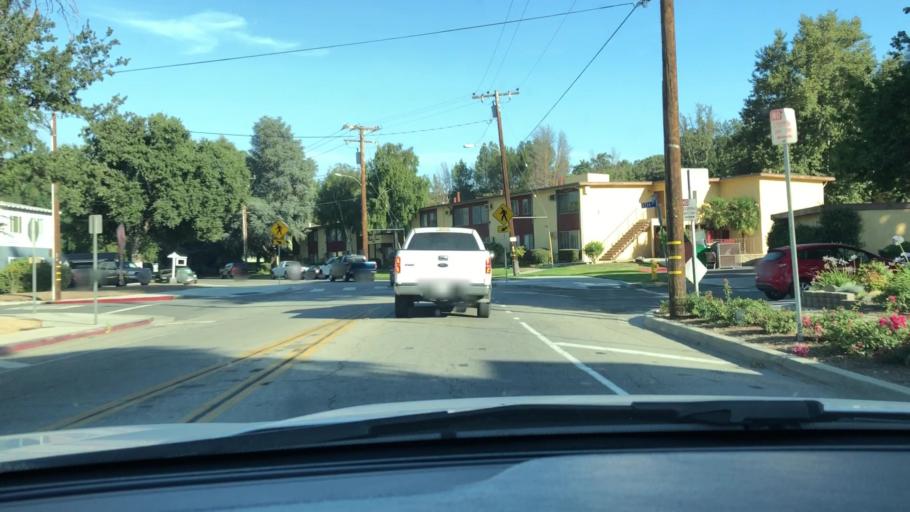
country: US
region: California
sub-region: Los Angeles County
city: Santa Clarita
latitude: 34.3793
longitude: -118.5324
